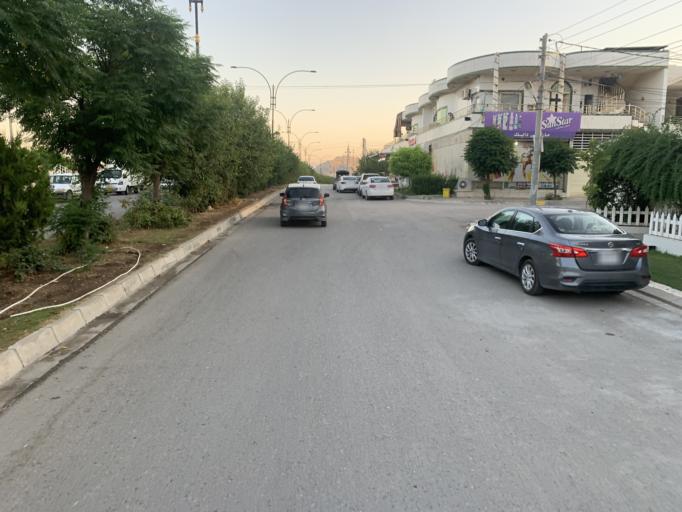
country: IQ
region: As Sulaymaniyah
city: Raniye
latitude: 36.2448
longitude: 44.8775
